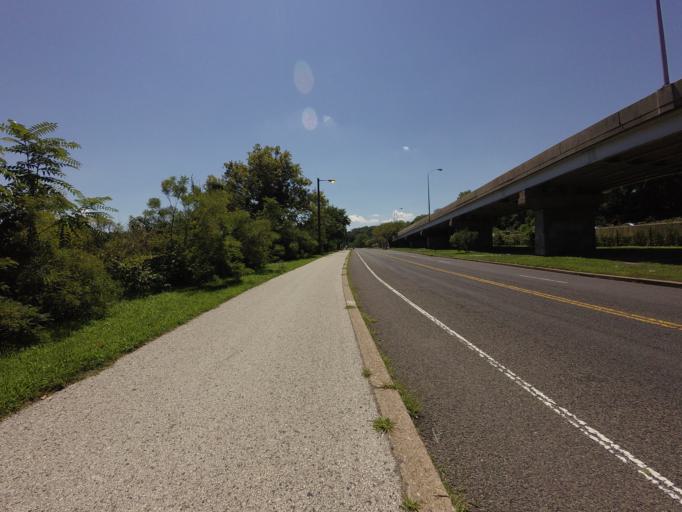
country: US
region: Pennsylvania
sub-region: Philadelphia County
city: Philadelphia
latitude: 39.9736
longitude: -75.1935
